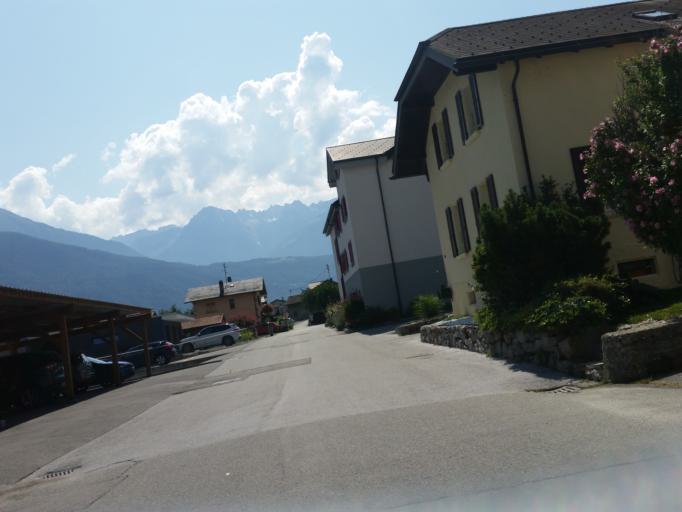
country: CH
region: Valais
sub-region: Martigny District
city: Fully
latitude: 46.1359
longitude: 7.1086
